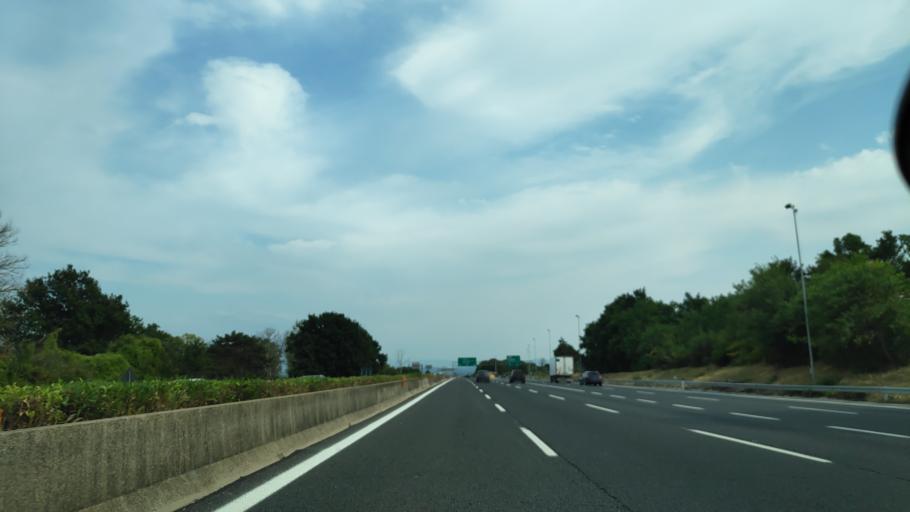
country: IT
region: Latium
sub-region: Citta metropolitana di Roma Capitale
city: Fiano Romano
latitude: 42.1692
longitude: 12.6123
